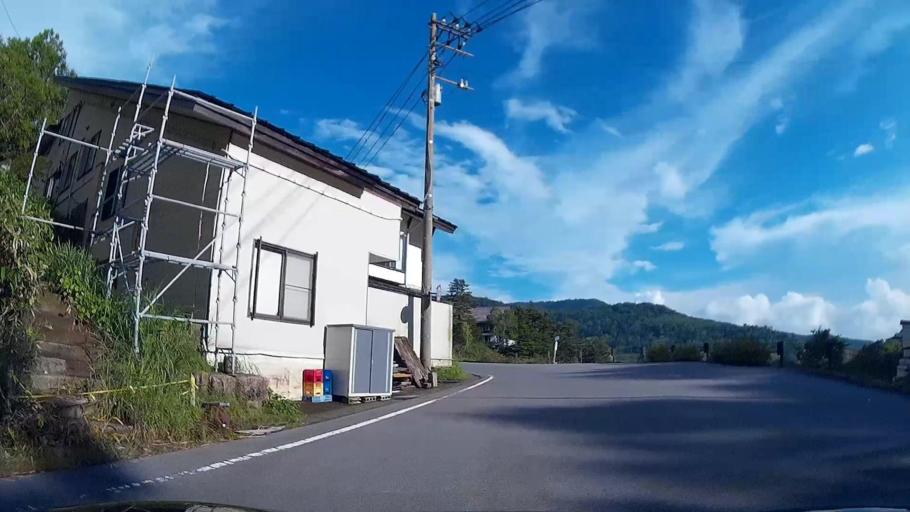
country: JP
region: Nagano
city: Nakano
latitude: 36.6398
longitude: 138.5098
